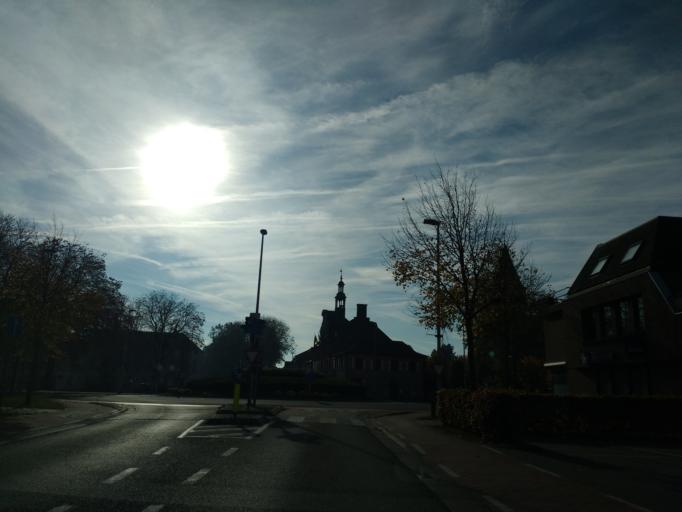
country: BE
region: Flanders
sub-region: Provincie Oost-Vlaanderen
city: Kaprijke
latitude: 51.2191
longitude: 3.6174
